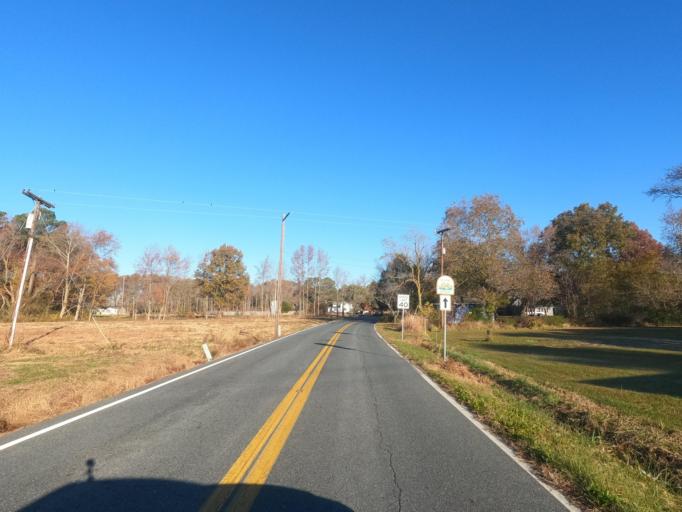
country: US
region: Maryland
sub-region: Somerset County
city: Crisfield
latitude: 38.0106
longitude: -75.8156
